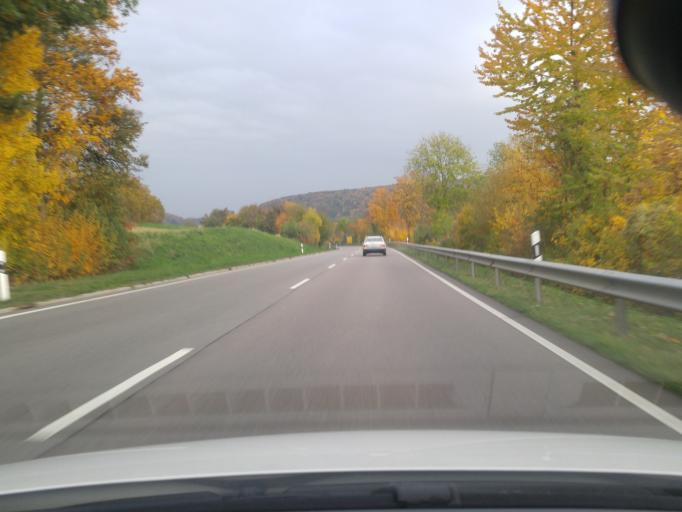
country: DE
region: Baden-Wuerttemberg
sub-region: Karlsruhe Region
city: Balzfeld
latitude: 49.2443
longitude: 8.8118
